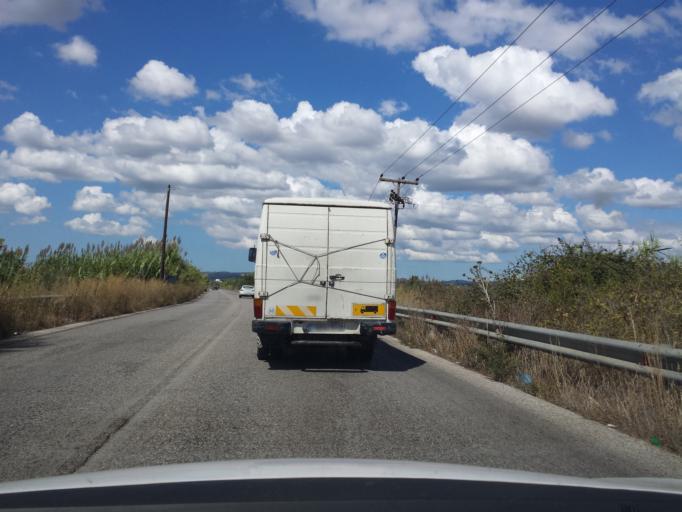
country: GR
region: West Greece
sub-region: Nomos Ileias
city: Epitalion
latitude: 37.6453
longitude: 21.4750
